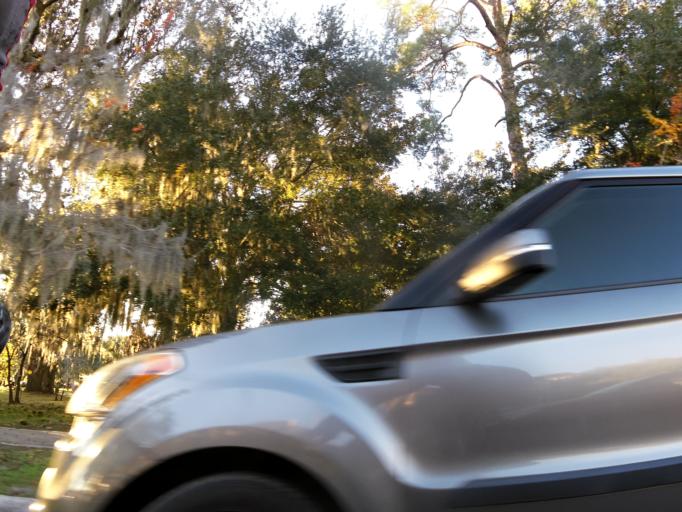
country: US
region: Florida
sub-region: Duval County
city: Jacksonville
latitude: 30.3160
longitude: -81.6803
